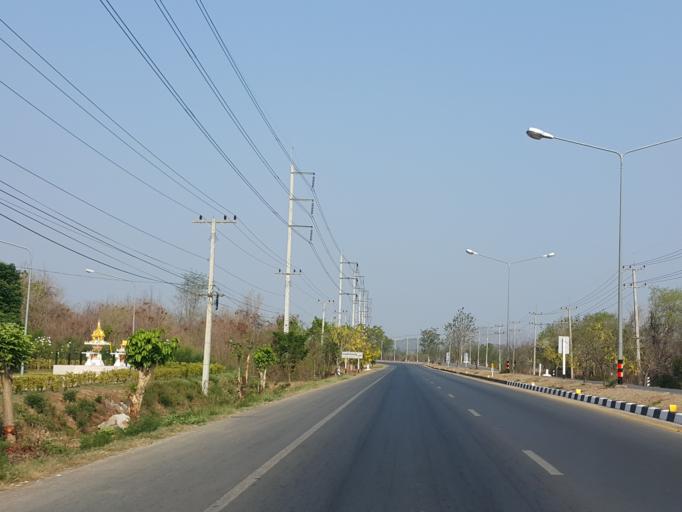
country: TH
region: Kanchanaburi
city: Kanchanaburi
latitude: 14.0677
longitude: 99.4092
